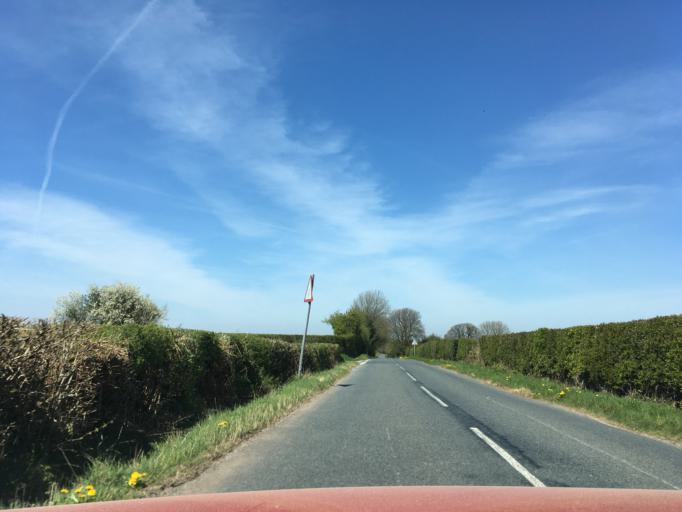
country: GB
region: Wales
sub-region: Newport
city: Llanvaches
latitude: 51.6561
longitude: -2.7900
